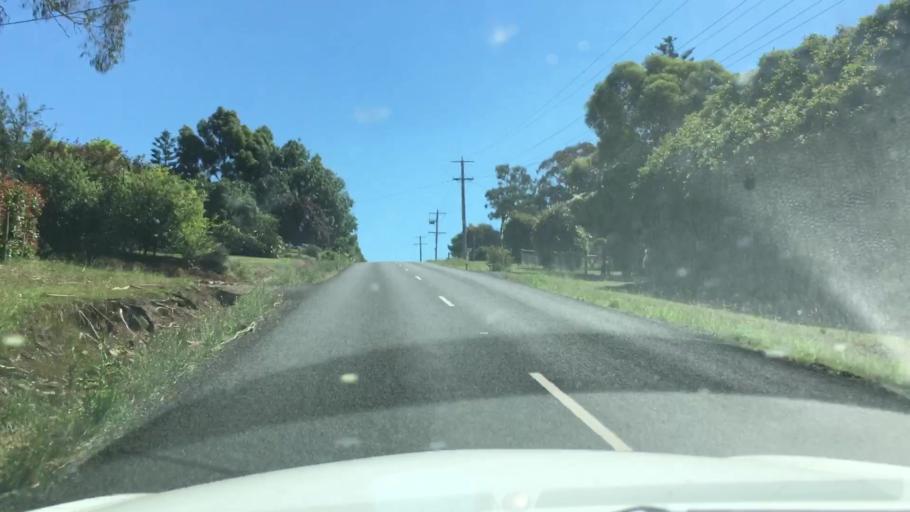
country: AU
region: Victoria
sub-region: Yarra Ranges
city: Mount Evelyn
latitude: -37.8079
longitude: 145.4331
